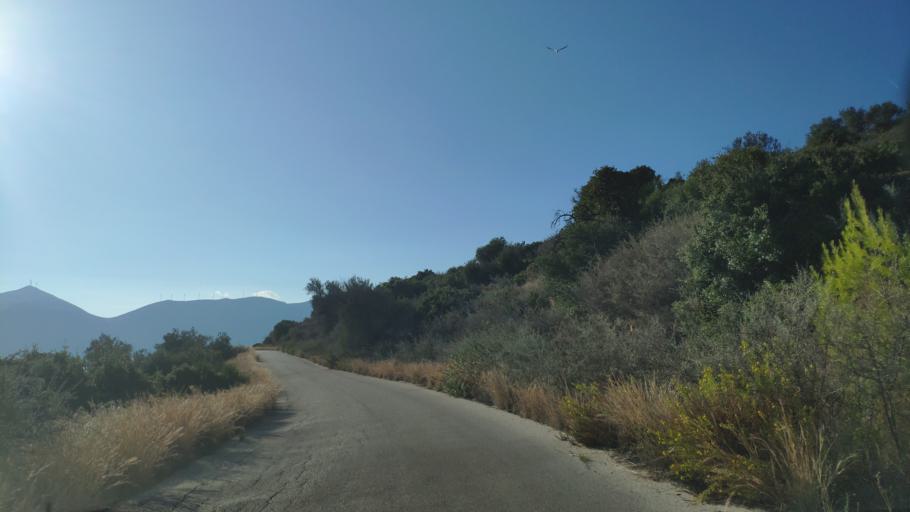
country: GR
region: Attica
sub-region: Nomos Piraios
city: Megalochori
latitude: 37.5816
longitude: 23.3505
